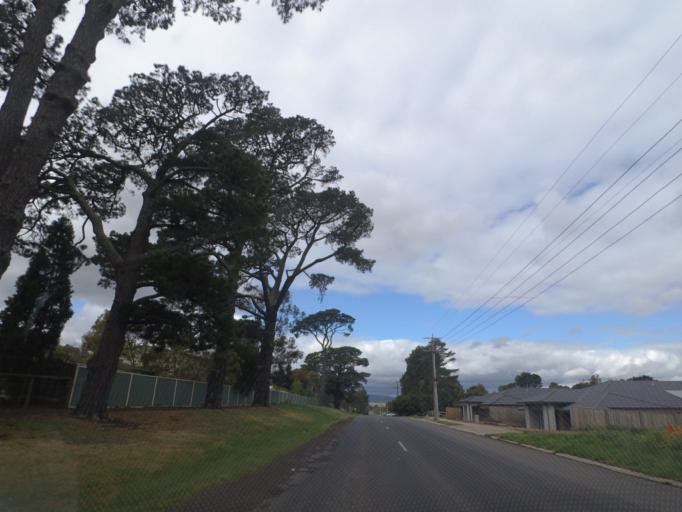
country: AU
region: Victoria
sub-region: Whittlesea
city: Whittlesea
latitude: -37.4049
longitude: 144.9652
